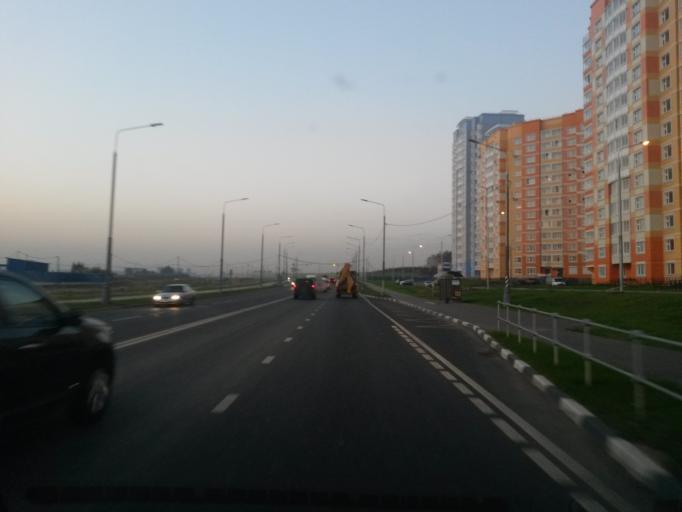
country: RU
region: Moskovskaya
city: Kommunarka
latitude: 55.5407
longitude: 37.4892
